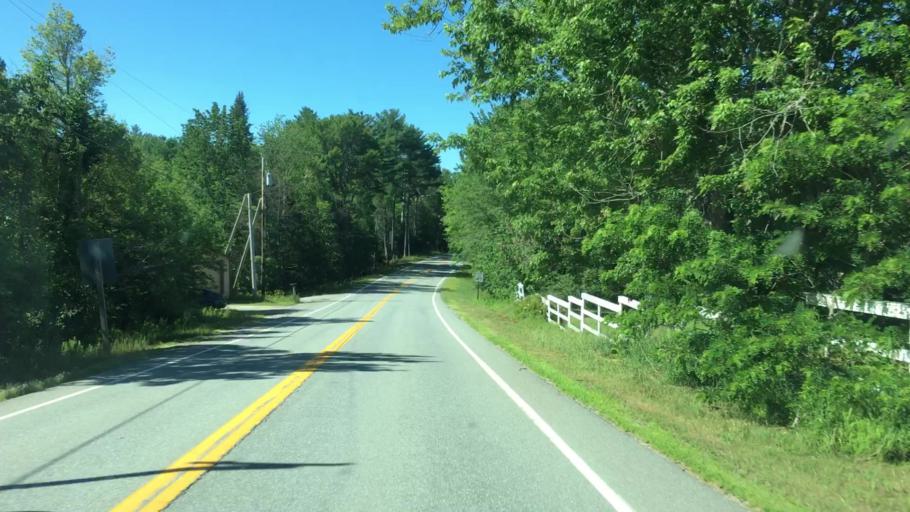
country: US
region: Maine
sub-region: Hancock County
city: Dedham
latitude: 44.6891
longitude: -68.6608
